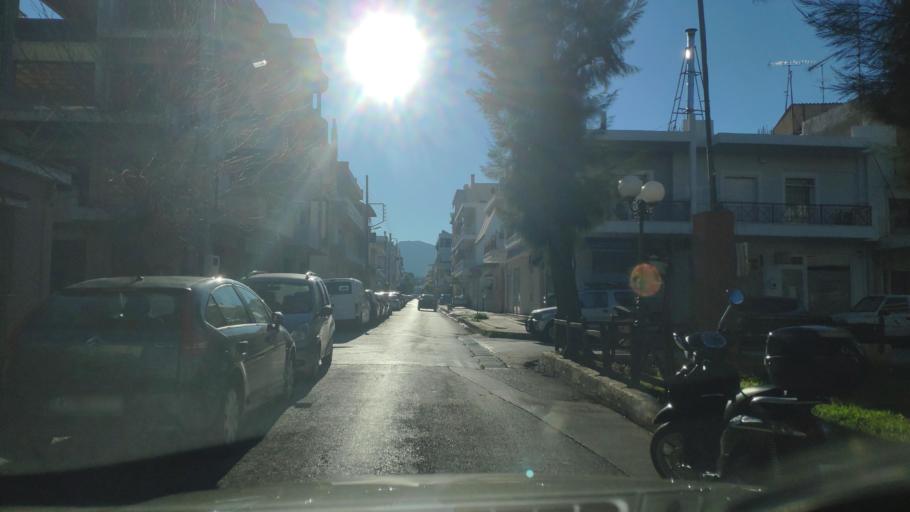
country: GR
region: Peloponnese
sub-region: Nomos Korinthias
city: Korinthos
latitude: 37.9379
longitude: 22.9250
